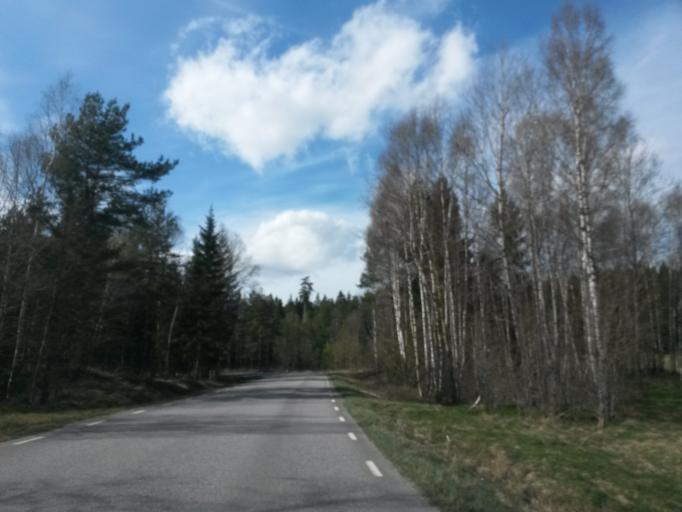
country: SE
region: Vaestra Goetaland
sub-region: Vargarda Kommun
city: Jonstorp
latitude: 57.9838
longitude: 12.7258
